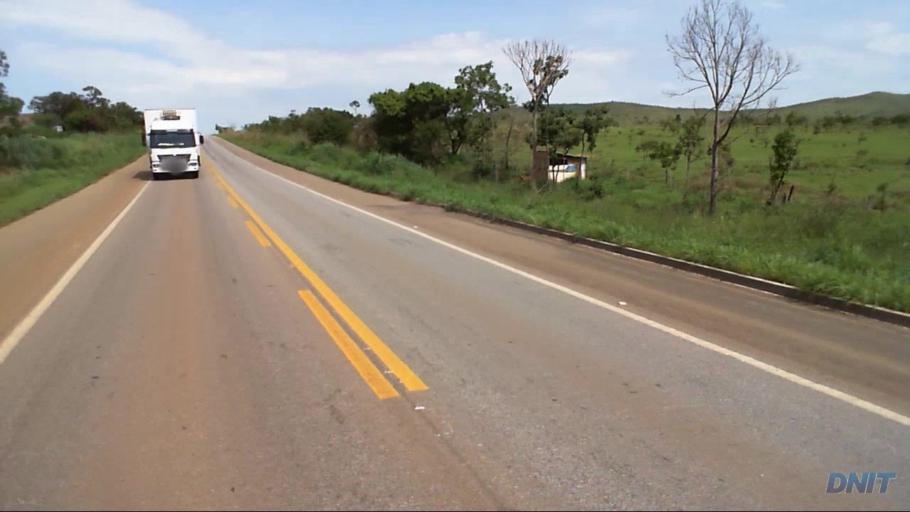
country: BR
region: Goias
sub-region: Barro Alto
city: Barro Alto
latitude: -15.1902
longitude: -48.7754
